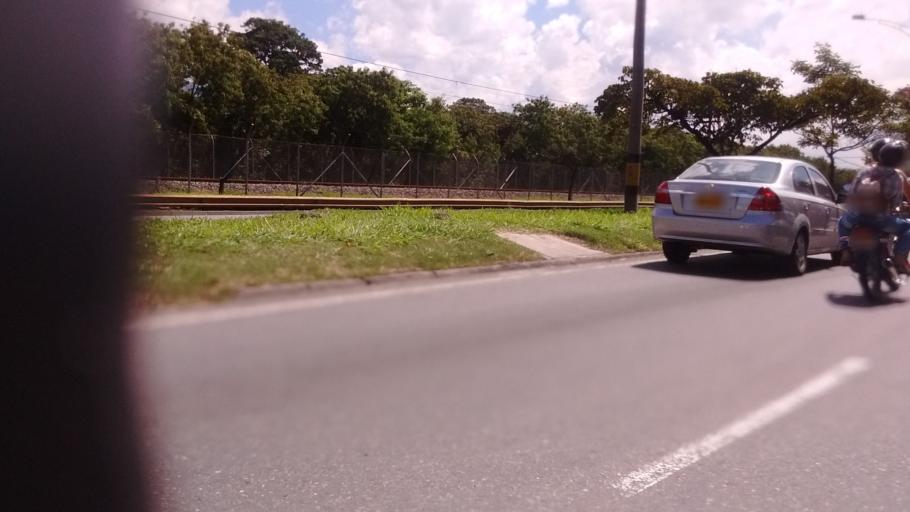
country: CO
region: Antioquia
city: Medellin
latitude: 6.2561
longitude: -75.5768
